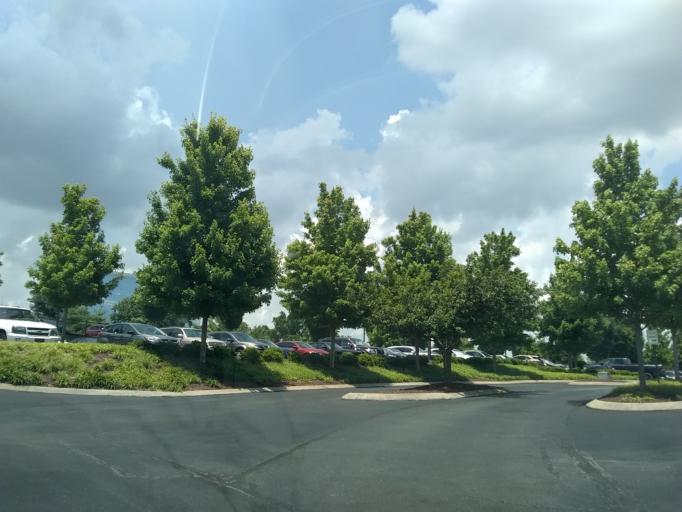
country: US
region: Tennessee
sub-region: Davidson County
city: Nashville
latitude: 36.1490
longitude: -86.6864
